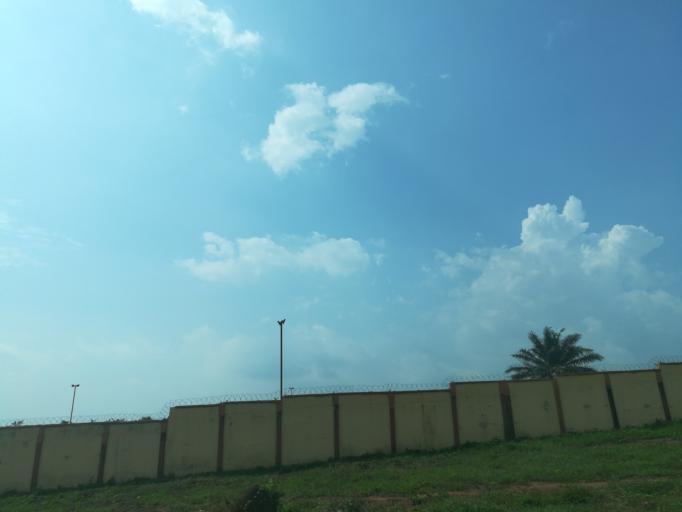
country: NG
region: Lagos
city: Ikorodu
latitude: 6.6197
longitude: 3.6552
